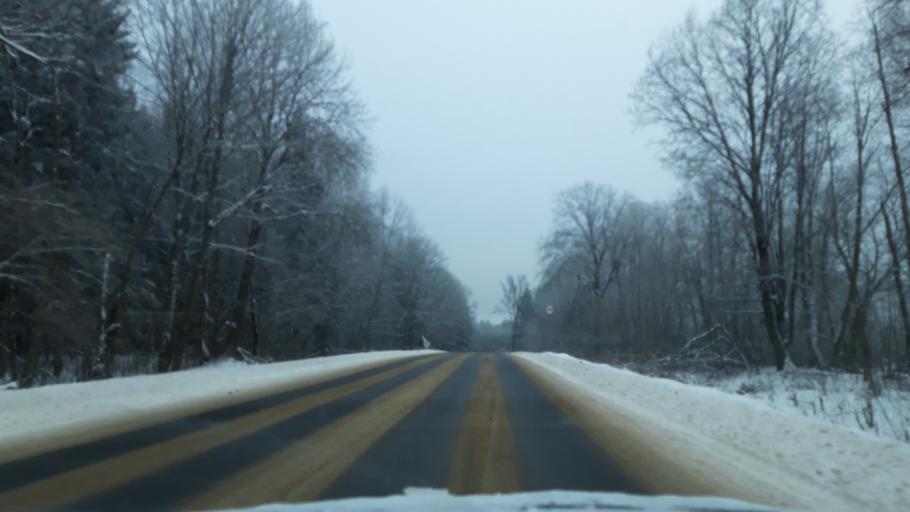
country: RU
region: Moskovskaya
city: Avtopoligon
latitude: 56.2781
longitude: 37.3715
